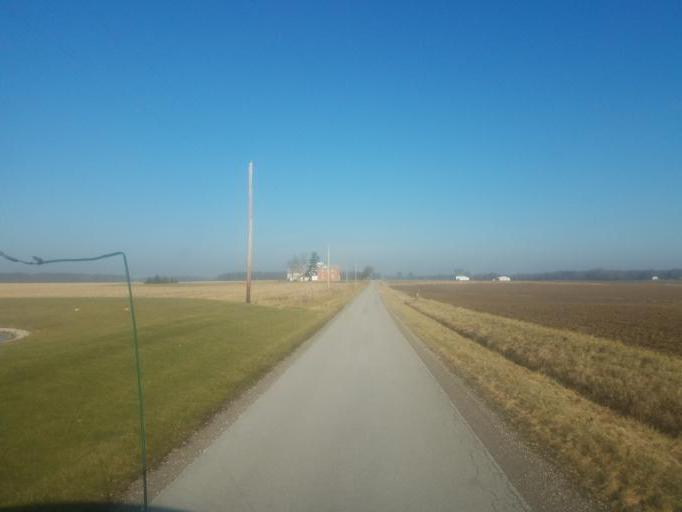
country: US
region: Ohio
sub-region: Huron County
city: Willard
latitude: 41.0296
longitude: -82.9391
